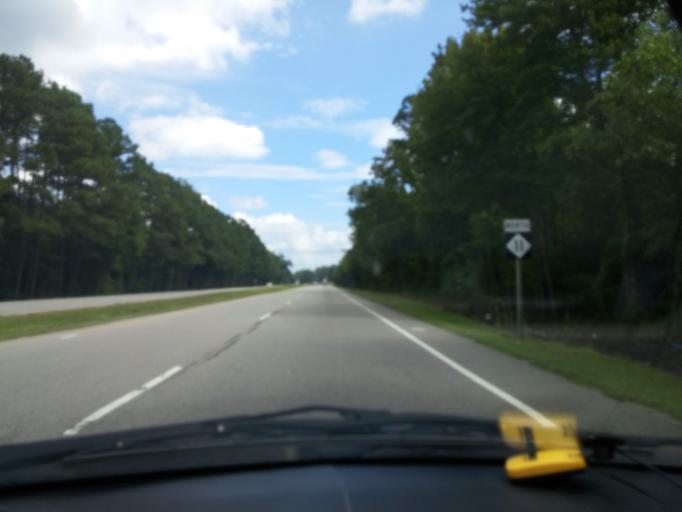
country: US
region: North Carolina
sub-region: Pitt County
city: Grifton
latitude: 35.3247
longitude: -77.5012
